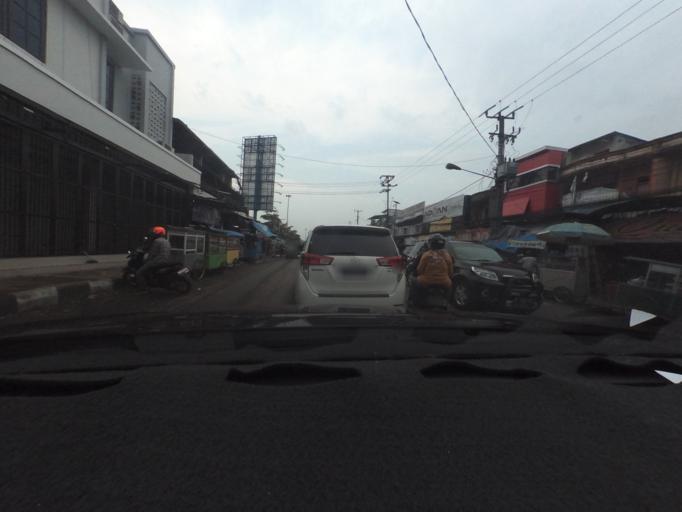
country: ID
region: West Java
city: Cicurug
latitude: -6.8866
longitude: 106.7795
